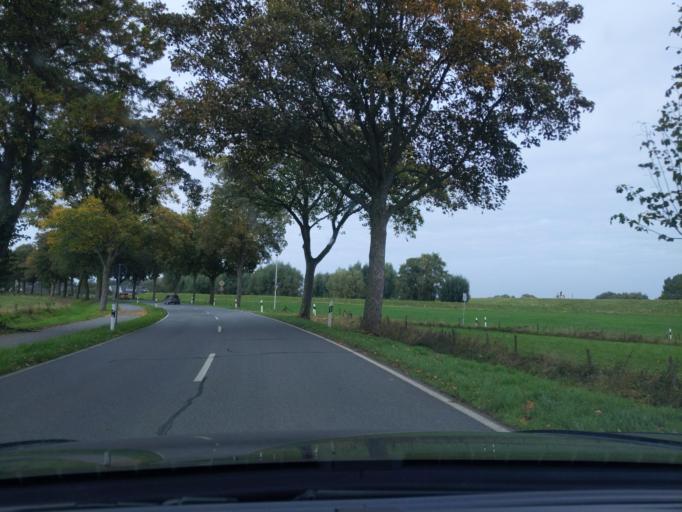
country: NL
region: Gelderland
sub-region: Gemeente Zevenaar
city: Zevenaar
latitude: 51.8593
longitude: 6.0660
